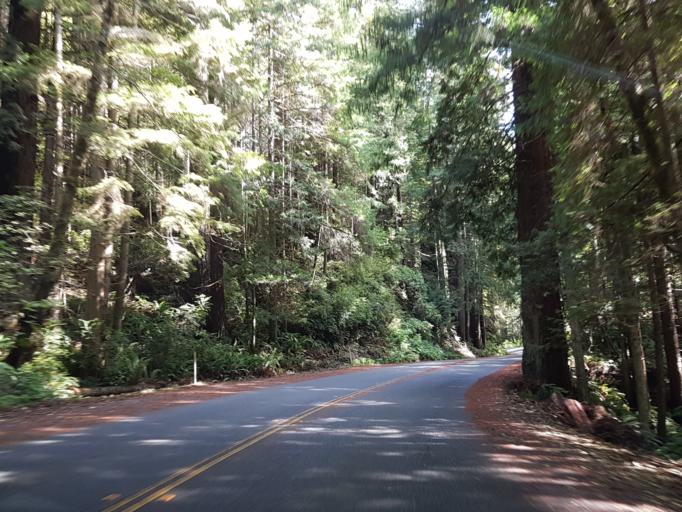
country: US
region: California
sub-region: Del Norte County
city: Bertsch-Oceanview
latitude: 41.4526
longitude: -124.0421
